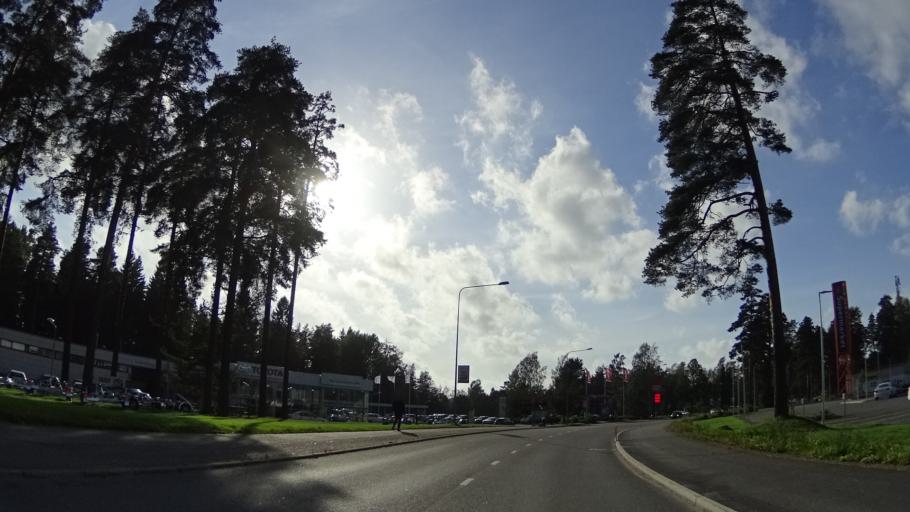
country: FI
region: Uusimaa
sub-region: Porvoo
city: Porvoo
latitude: 60.3990
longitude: 25.6870
